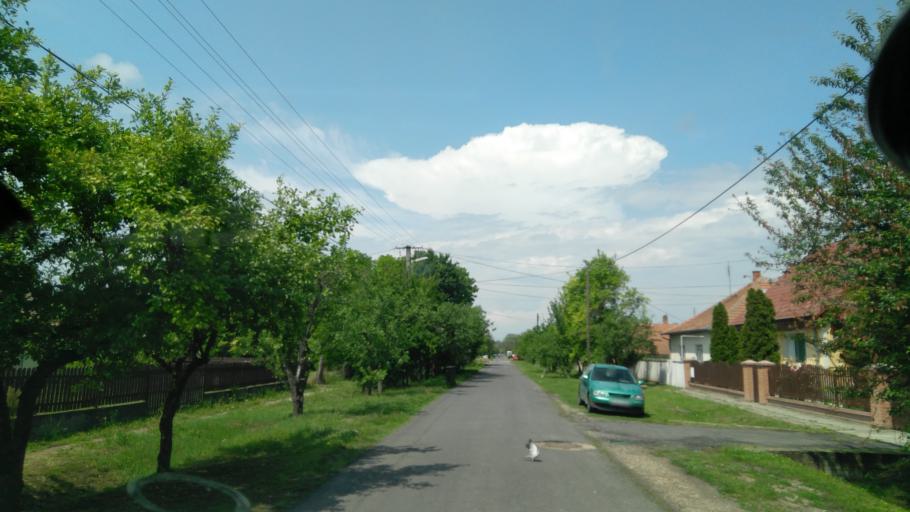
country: HU
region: Bekes
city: Bekes
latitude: 46.7572
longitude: 21.1463
